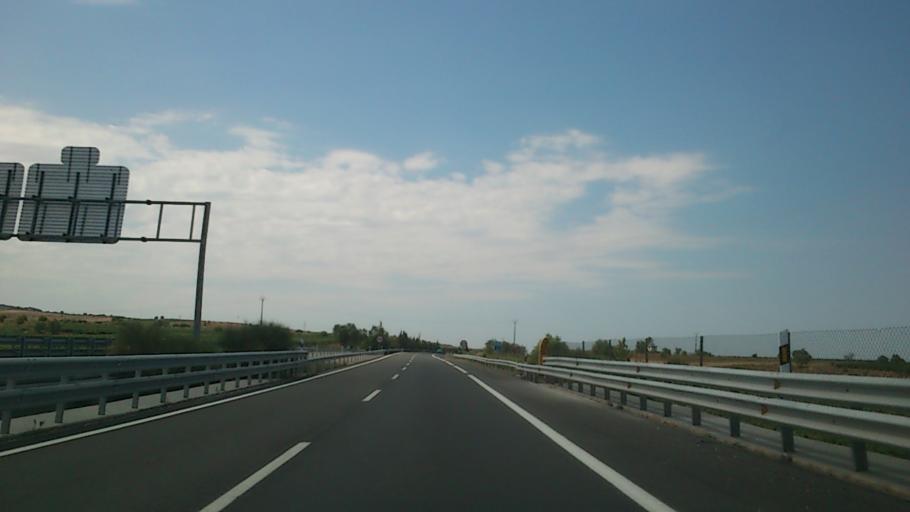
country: ES
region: La Rioja
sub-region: Provincia de La Rioja
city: Navarrete
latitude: 42.4477
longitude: -2.5657
